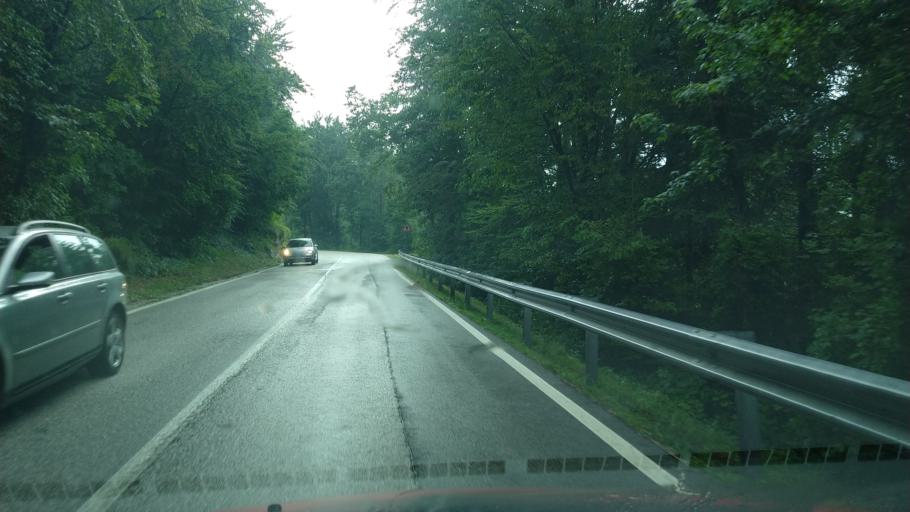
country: IT
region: Veneto
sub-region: Provincia di Vicenza
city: Tonezza del Cimone
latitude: 45.8535
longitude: 11.3549
